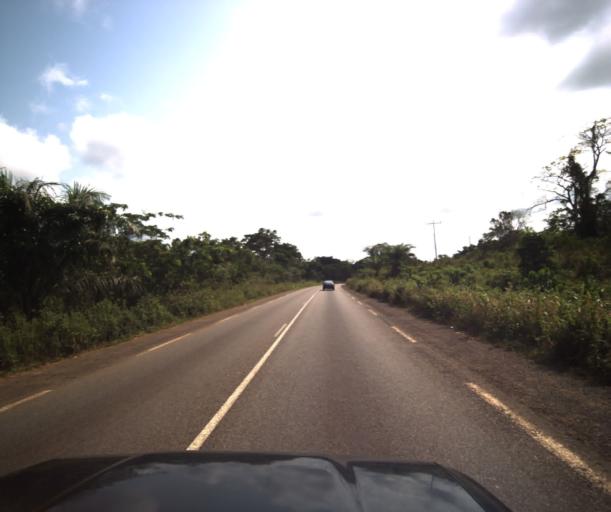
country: CM
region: Littoral
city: Edea
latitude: 3.7722
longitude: 10.1888
